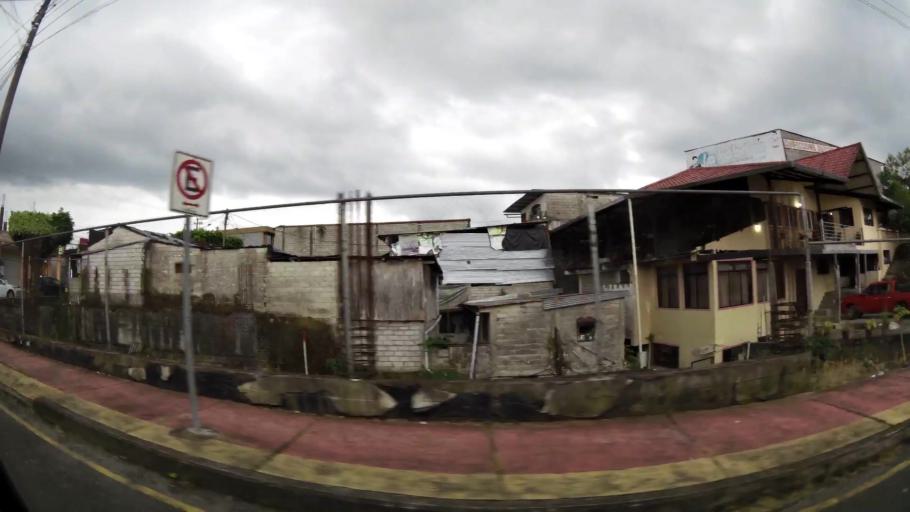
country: EC
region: Pastaza
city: Puyo
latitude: -1.4898
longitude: -77.9985
